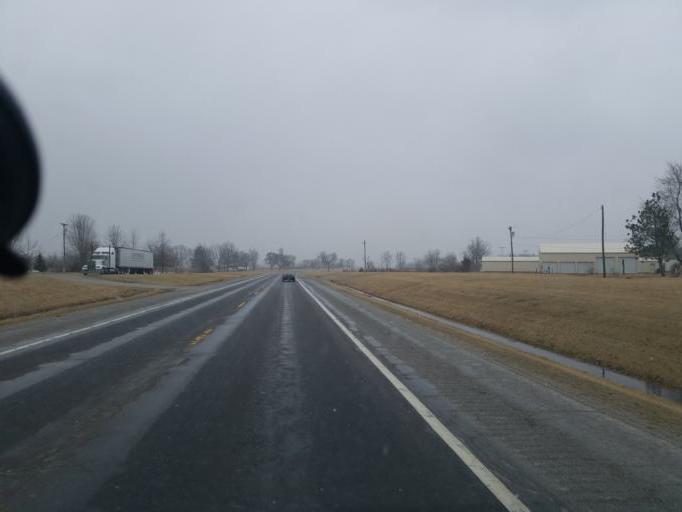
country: US
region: Missouri
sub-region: Schuyler County
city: Lancaster
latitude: 40.4111
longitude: -92.5621
